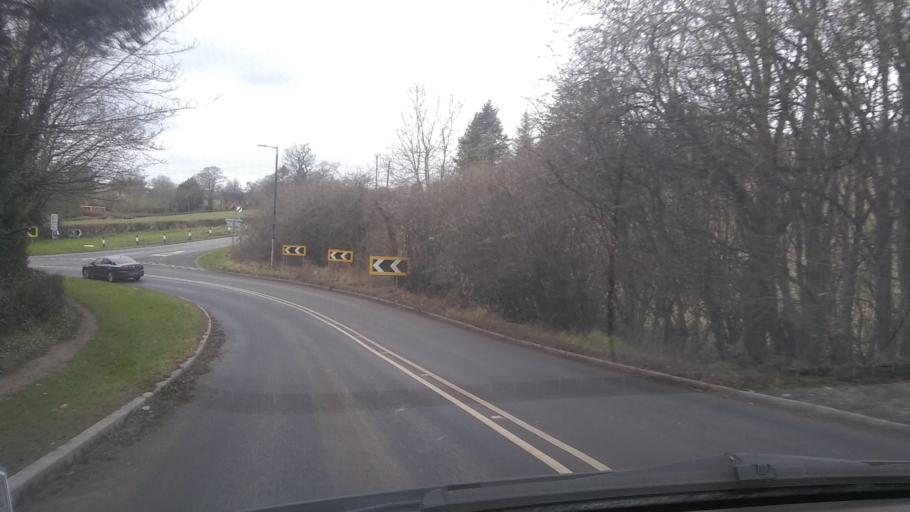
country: GB
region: England
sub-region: Shropshire
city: Cleobury Mortimer
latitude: 52.3845
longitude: -2.4703
